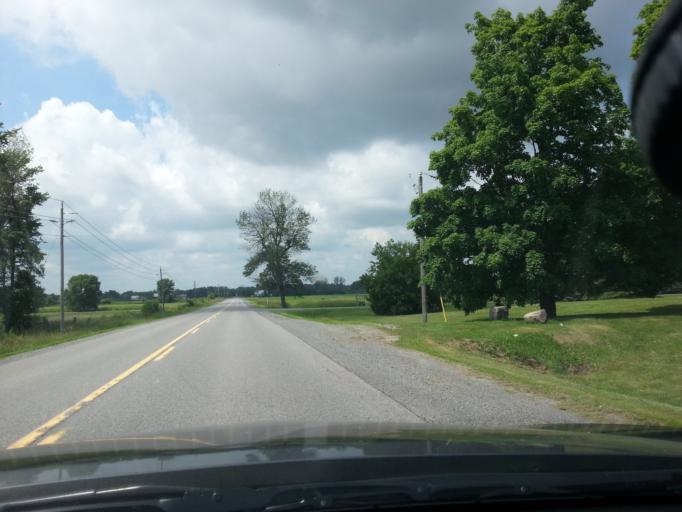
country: CA
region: Ontario
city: Bells Corners
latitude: 45.2526
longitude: -75.6845
